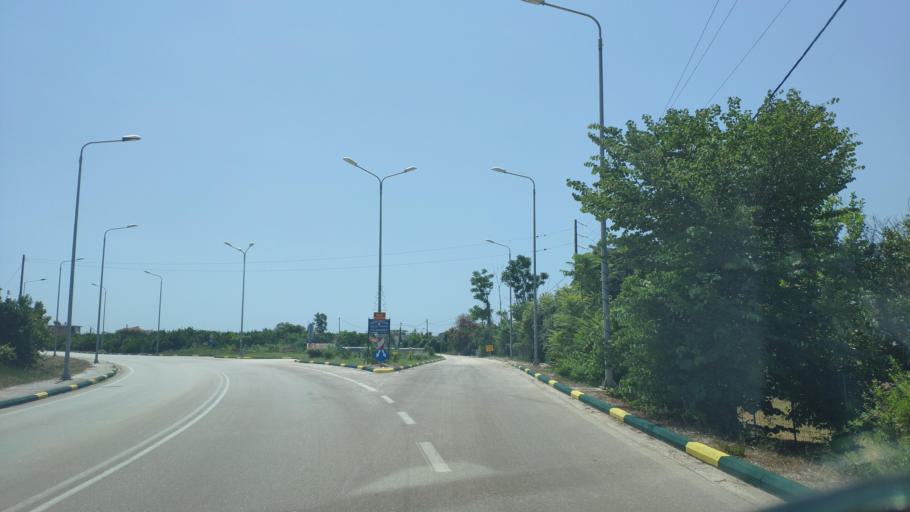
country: GR
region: Epirus
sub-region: Nomos Artas
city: Arta
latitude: 39.1411
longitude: 20.9807
